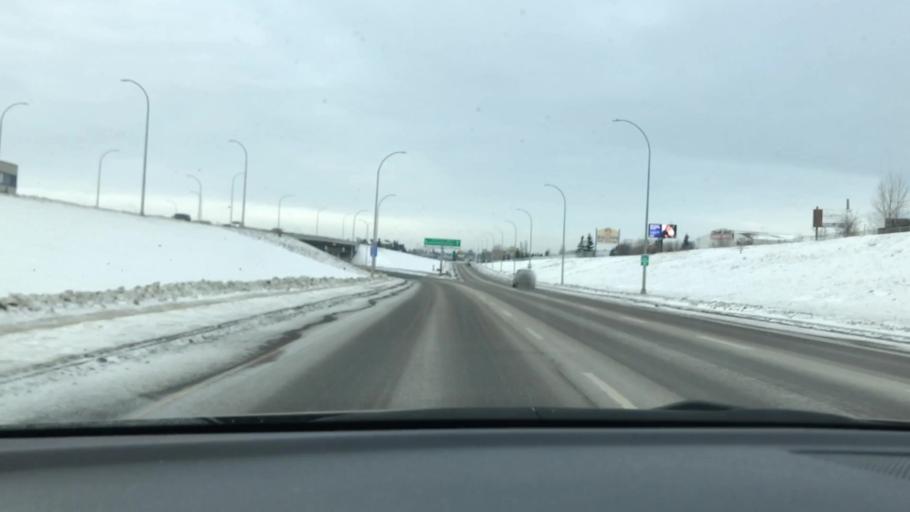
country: CA
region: Alberta
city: Edmonton
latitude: 53.5155
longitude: -113.4275
